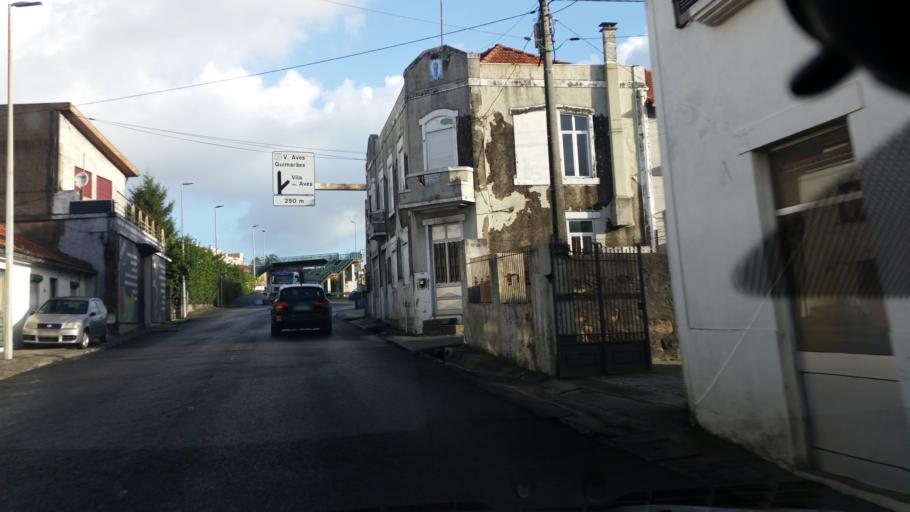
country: PT
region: Porto
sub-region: Santo Tirso
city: Negrelos
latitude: 41.3591
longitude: -8.4019
